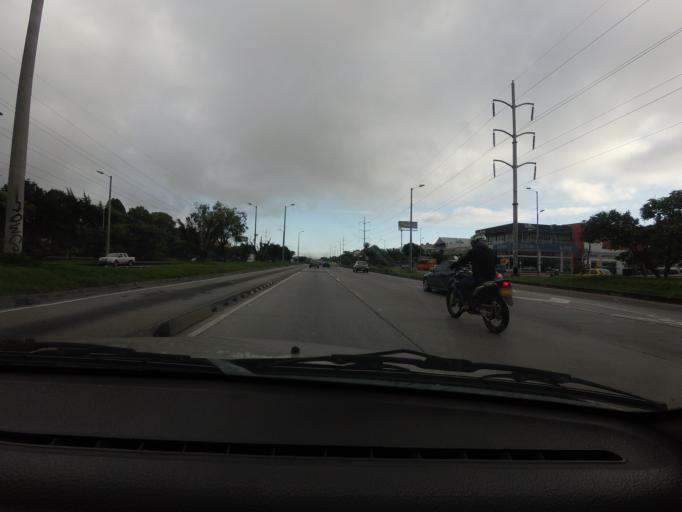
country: CO
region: Bogota D.C.
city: Barrio San Luis
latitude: 4.7284
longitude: -74.0502
